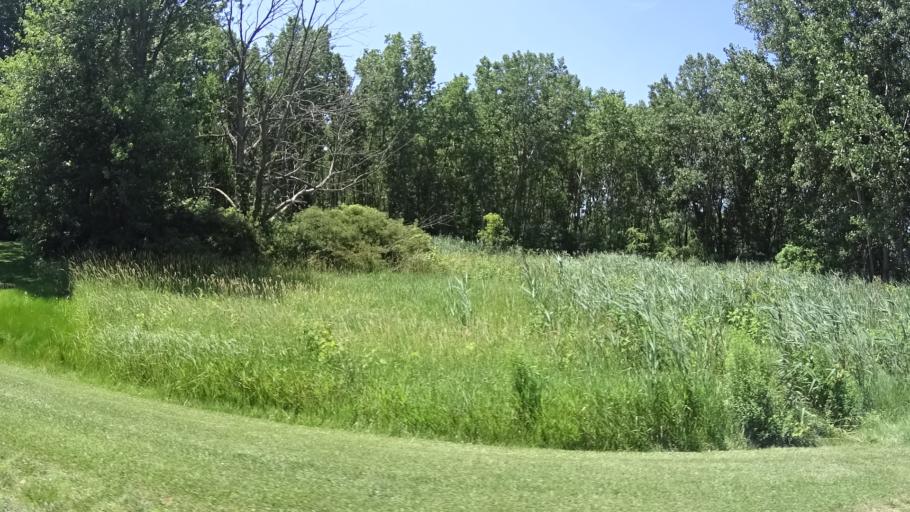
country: US
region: Ohio
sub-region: Erie County
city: Sandusky
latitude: 41.4529
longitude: -82.7809
